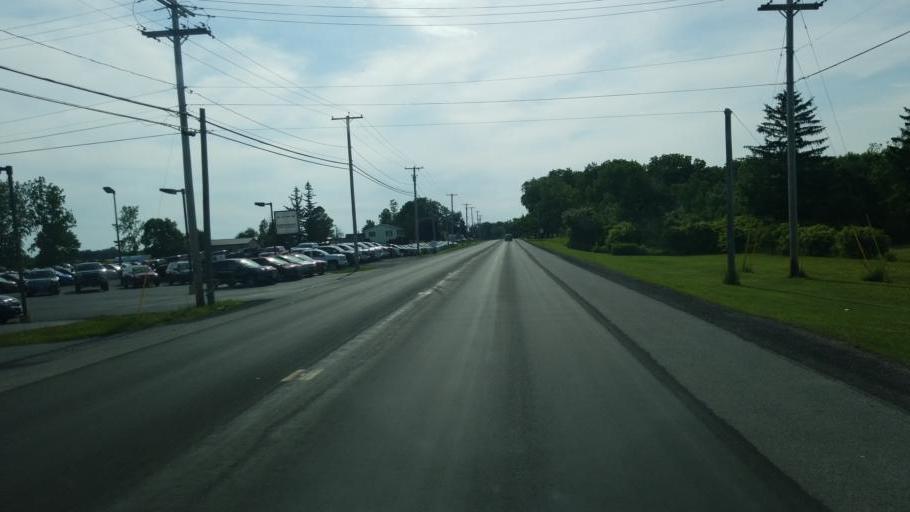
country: US
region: New York
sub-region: Genesee County
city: Le Roy
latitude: 42.9794
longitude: -78.0192
